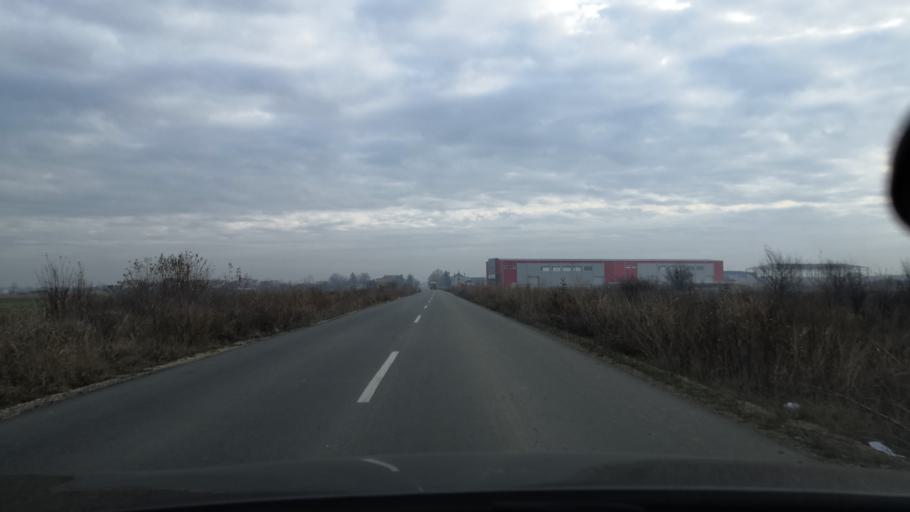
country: RS
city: Ugrinovci
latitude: 44.8806
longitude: 20.1616
